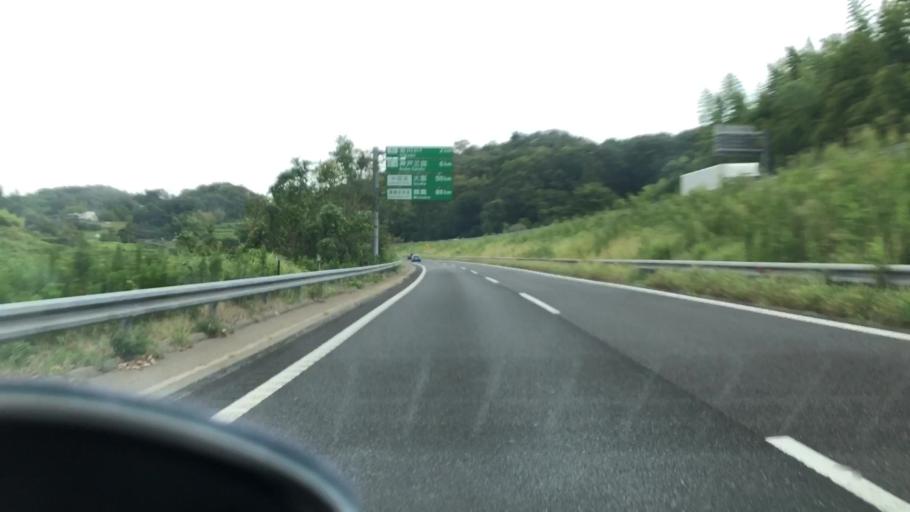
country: JP
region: Hyogo
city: Sandacho
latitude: 34.8900
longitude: 135.1299
